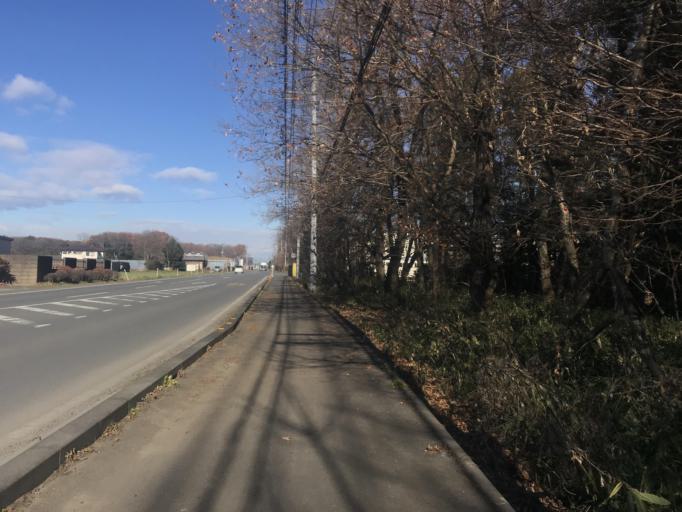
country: JP
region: Ibaraki
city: Yuki
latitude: 36.3440
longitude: 139.8788
